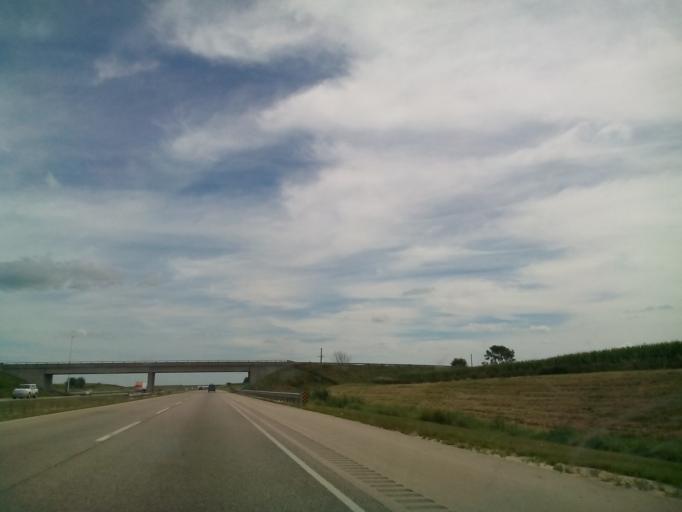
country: US
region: Illinois
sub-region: DeKalb County
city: Malta
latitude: 41.8994
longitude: -88.9275
